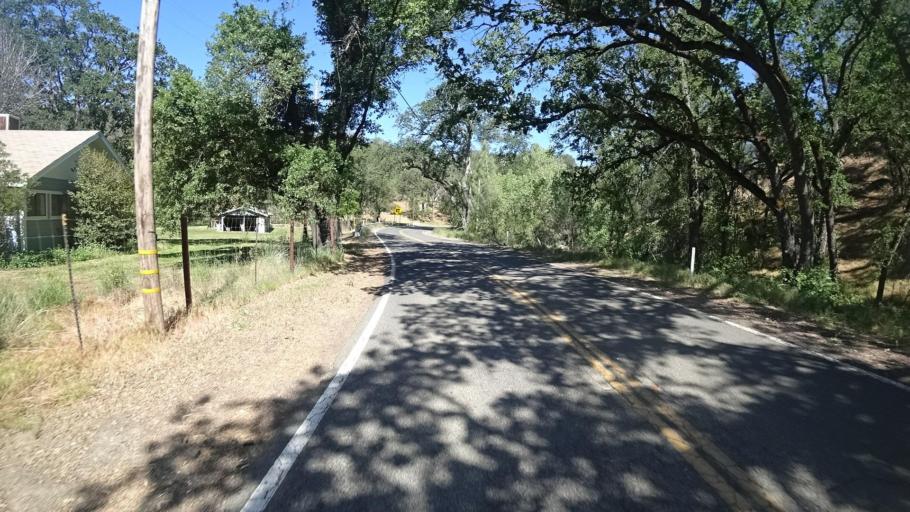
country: US
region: California
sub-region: Lake County
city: Lower Lake
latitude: 38.9045
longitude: -122.5780
